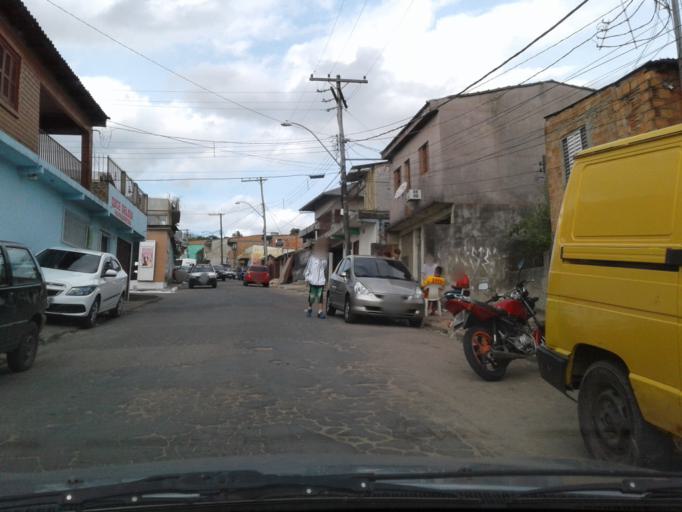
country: BR
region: Rio Grande do Sul
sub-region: Porto Alegre
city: Porto Alegre
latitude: -30.0499
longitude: -51.1523
